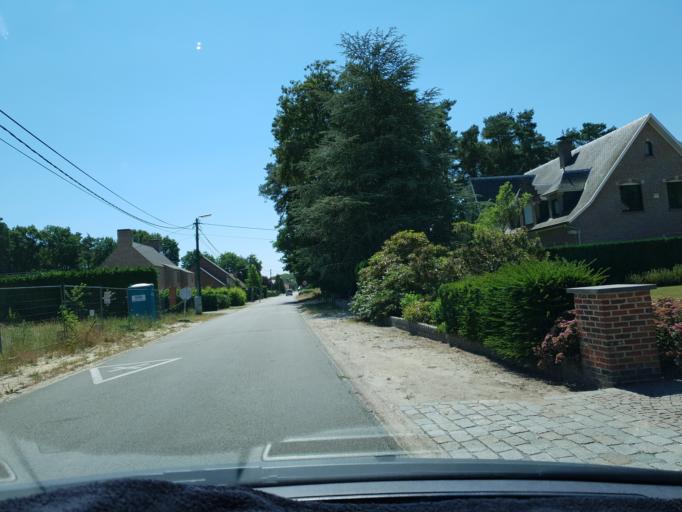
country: BE
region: Flanders
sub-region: Provincie Vlaams-Brabant
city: Tremelo
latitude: 50.9931
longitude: 4.7393
